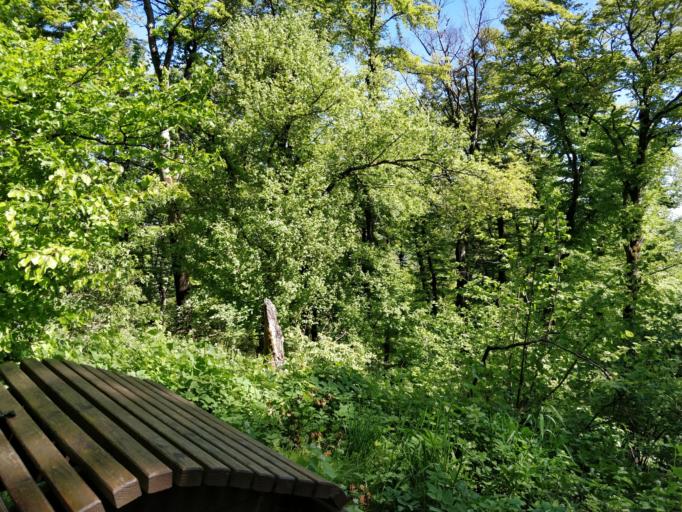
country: DE
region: Rheinland-Pfalz
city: Mosbruch
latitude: 50.2739
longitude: 6.9532
